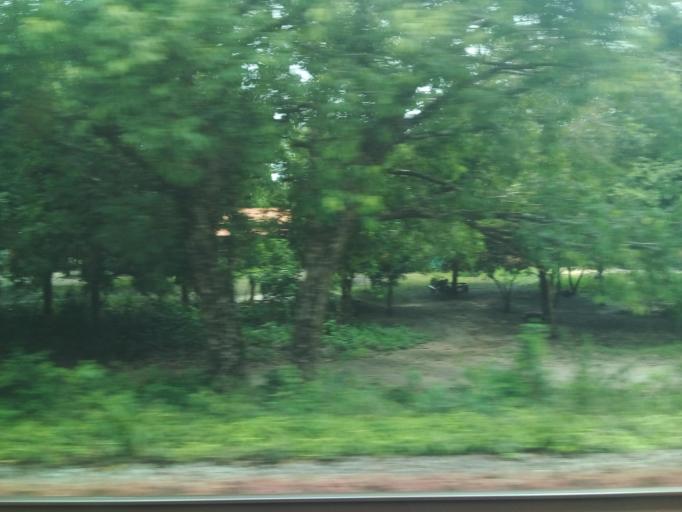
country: BR
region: Maranhao
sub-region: Arari
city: Arari
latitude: -3.5693
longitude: -44.7774
